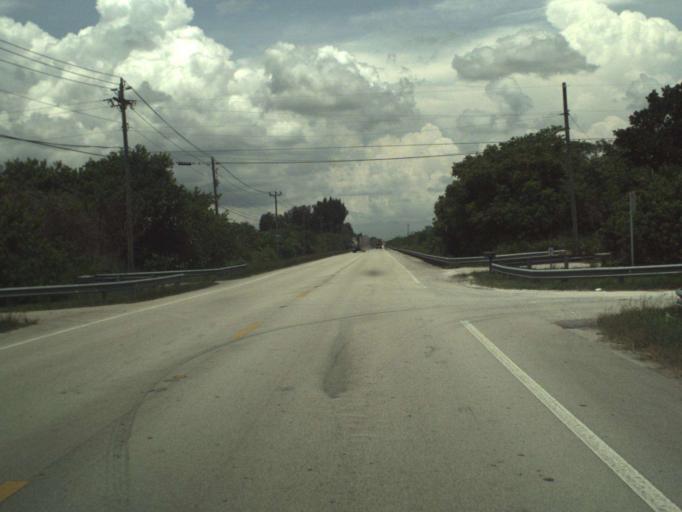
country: US
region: Florida
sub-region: Saint Lucie County
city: Lakewood Park
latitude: 27.5213
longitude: -80.4229
